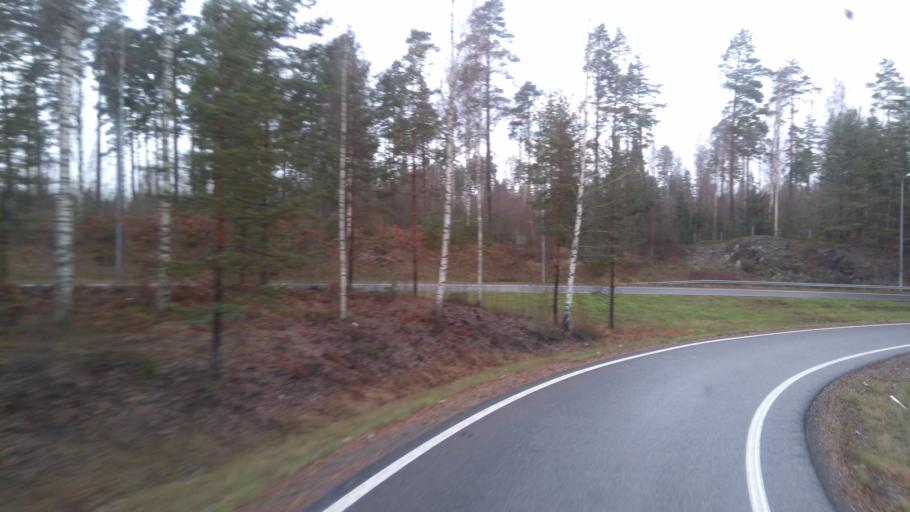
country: FI
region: Uusimaa
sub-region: Porvoo
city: Porvoo
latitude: 60.4194
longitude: 25.7035
